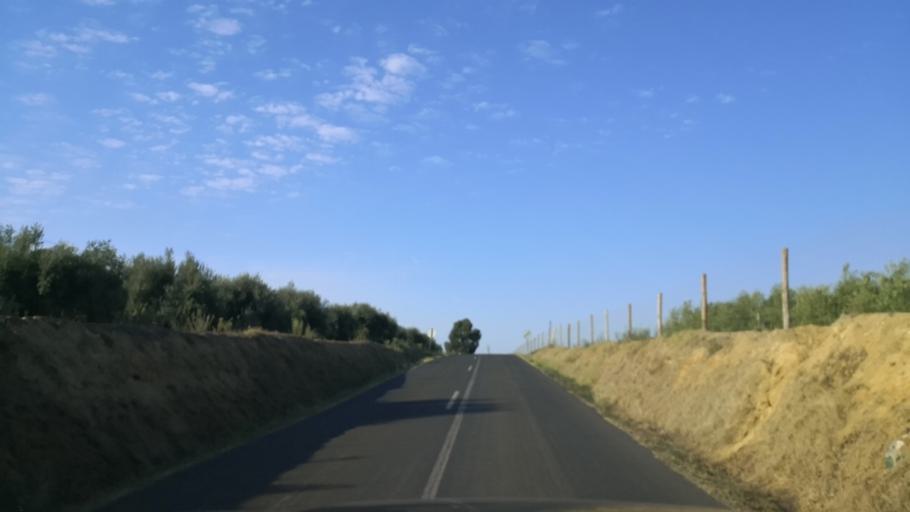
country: PT
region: Santarem
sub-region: Santarem
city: Santarem
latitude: 39.2755
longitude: -8.6608
